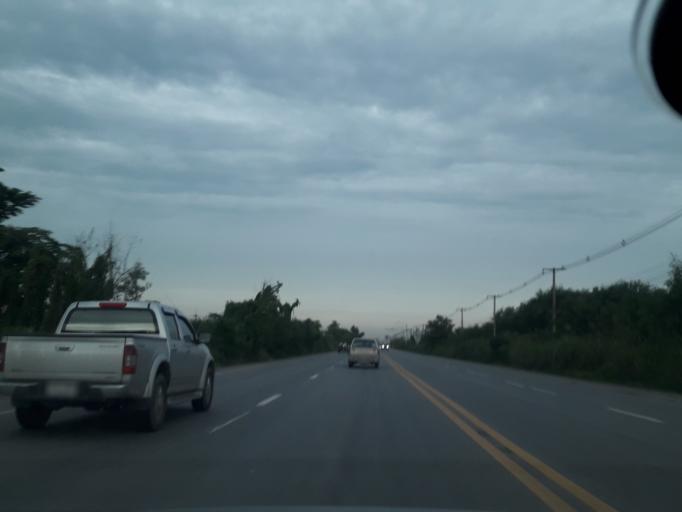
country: TH
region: Pathum Thani
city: Ban Rangsit
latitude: 14.0671
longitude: 100.7471
